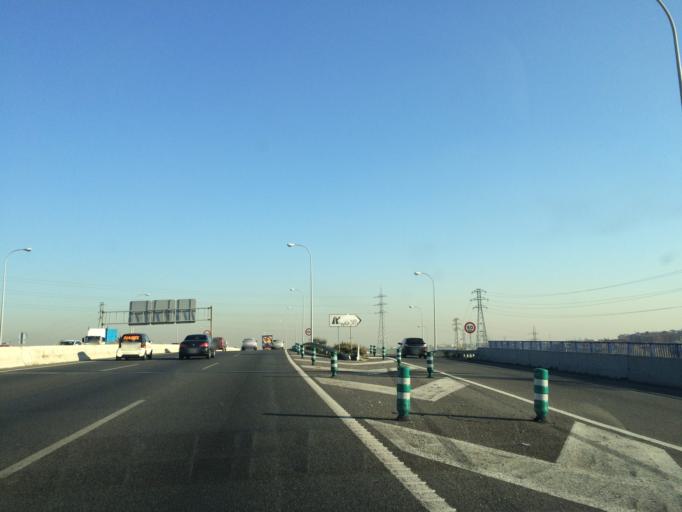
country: ES
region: Madrid
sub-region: Provincia de Madrid
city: Alcorcon
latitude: 40.3615
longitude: -3.8099
